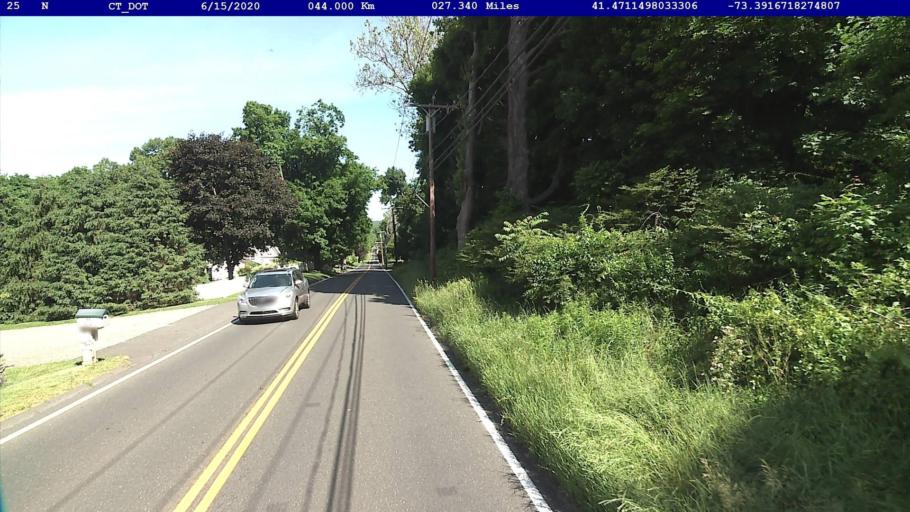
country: US
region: Connecticut
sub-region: Fairfield County
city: Danbury
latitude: 41.4712
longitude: -73.3917
